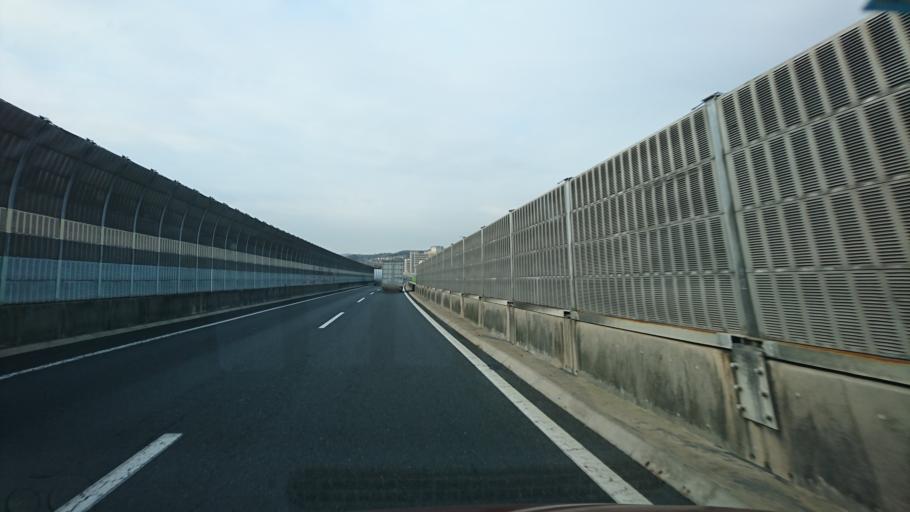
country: JP
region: Okayama
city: Okayama-shi
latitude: 34.7091
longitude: 133.9107
